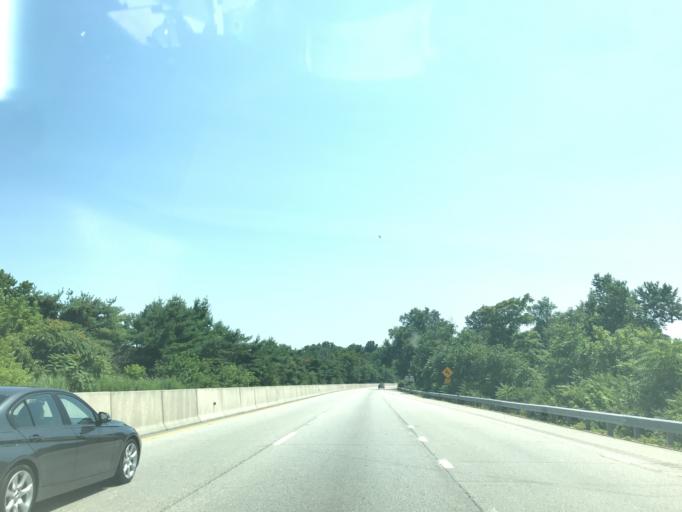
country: US
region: Pennsylvania
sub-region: Chester County
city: West Chester
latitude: 39.9645
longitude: -75.5807
